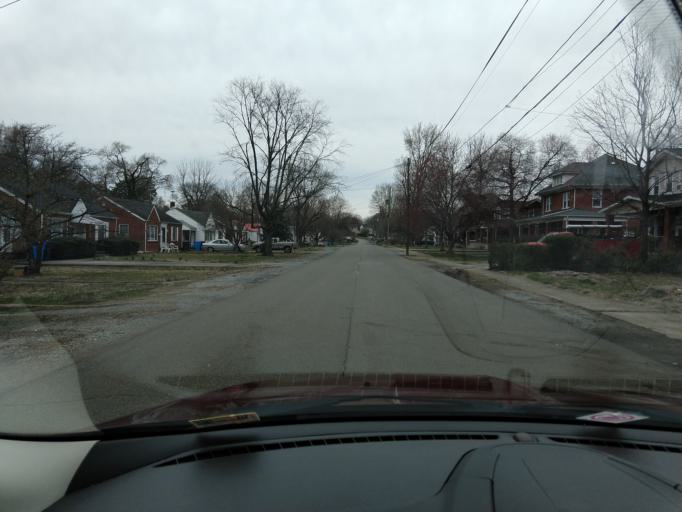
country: US
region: Virginia
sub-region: City of Roanoke
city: Roanoke
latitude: 37.3027
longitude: -79.9366
